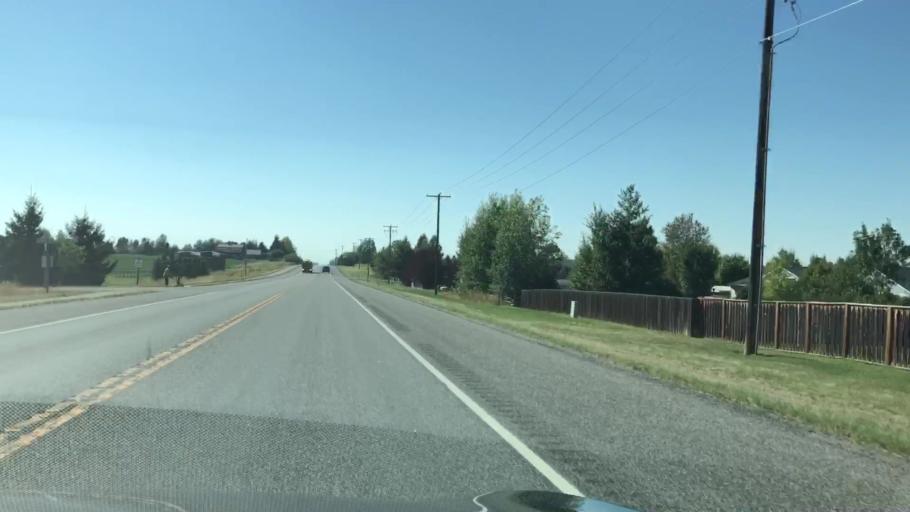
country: US
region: Montana
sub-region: Gallatin County
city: Belgrade
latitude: 45.7293
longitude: -111.1297
